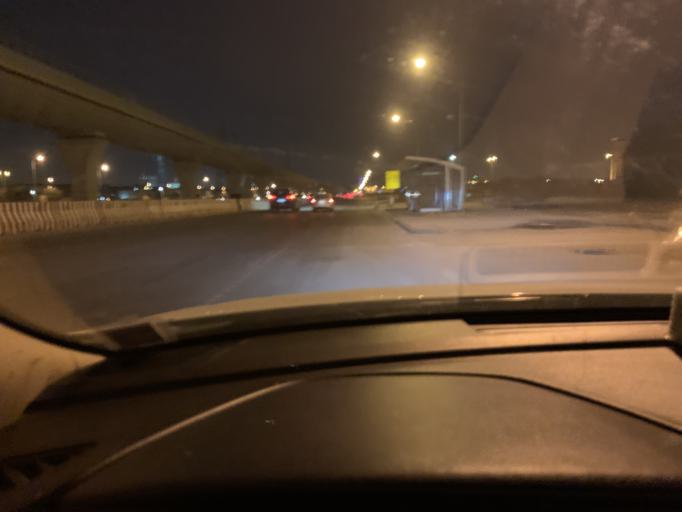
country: SA
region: Ar Riyad
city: Riyadh
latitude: 24.7914
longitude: 46.6717
